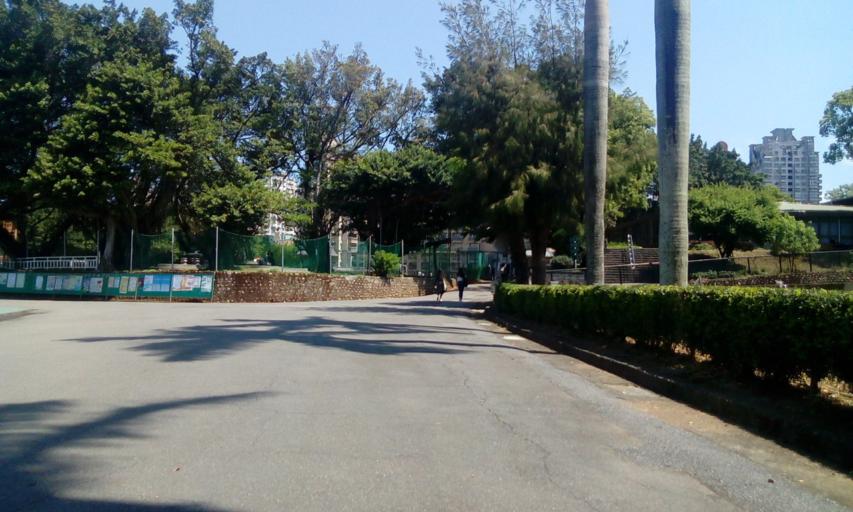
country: TW
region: Taipei
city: Taipei
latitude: 25.1764
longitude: 121.4351
